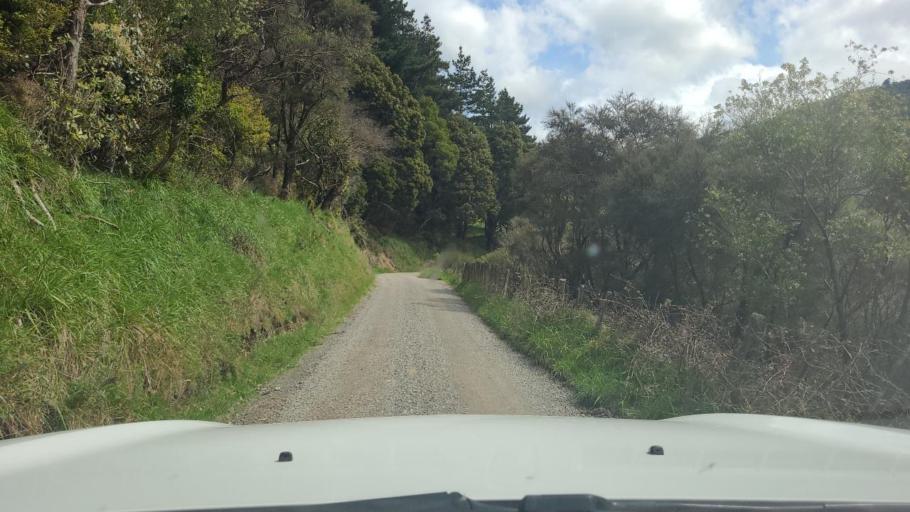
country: NZ
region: Wellington
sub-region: Masterton District
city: Masterton
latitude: -40.9316
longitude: 175.4981
